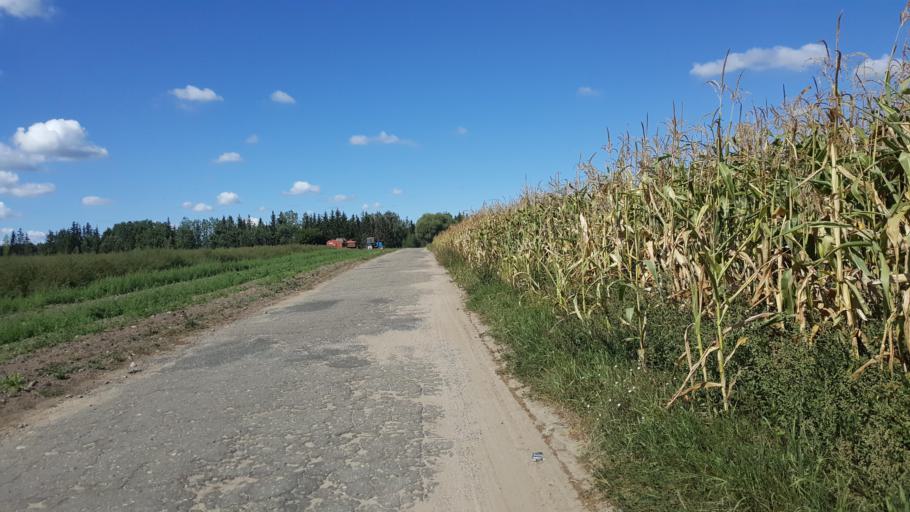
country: BY
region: Brest
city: Vysokaye
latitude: 52.3357
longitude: 23.3388
